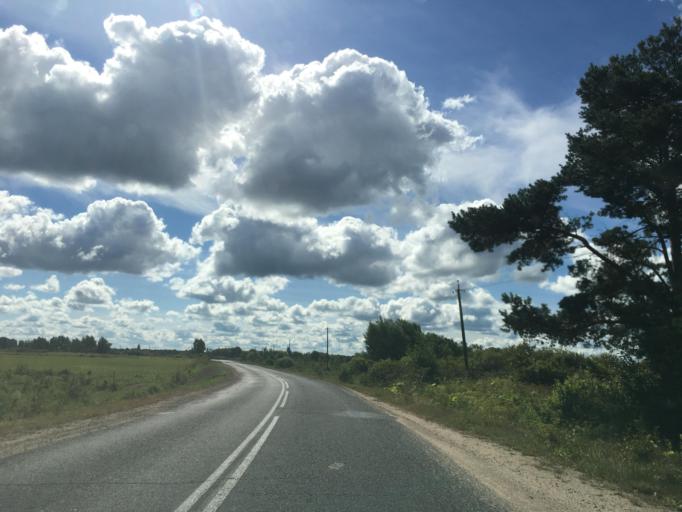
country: RU
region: Pskov
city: Pskov
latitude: 57.7360
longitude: 28.1547
